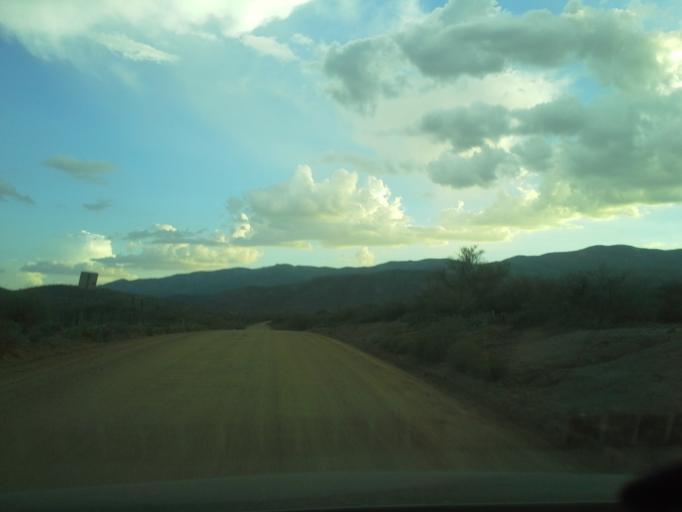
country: US
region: Arizona
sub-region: Yavapai County
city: Cordes Lakes
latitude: 34.1992
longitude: -112.1549
